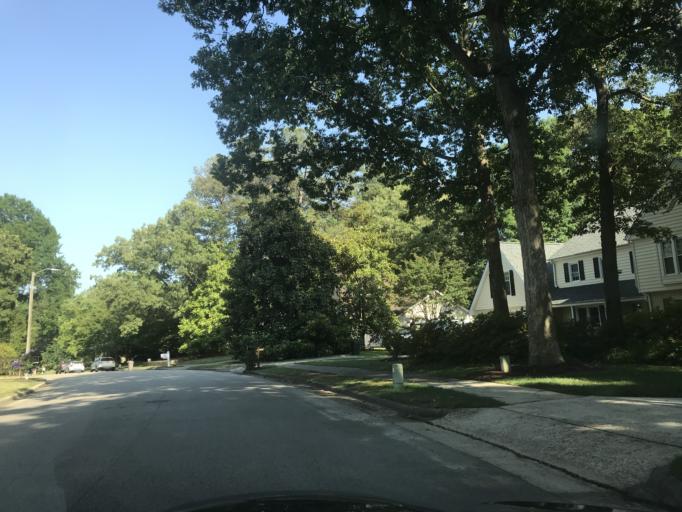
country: US
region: North Carolina
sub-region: Wake County
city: West Raleigh
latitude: 35.8720
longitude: -78.6154
